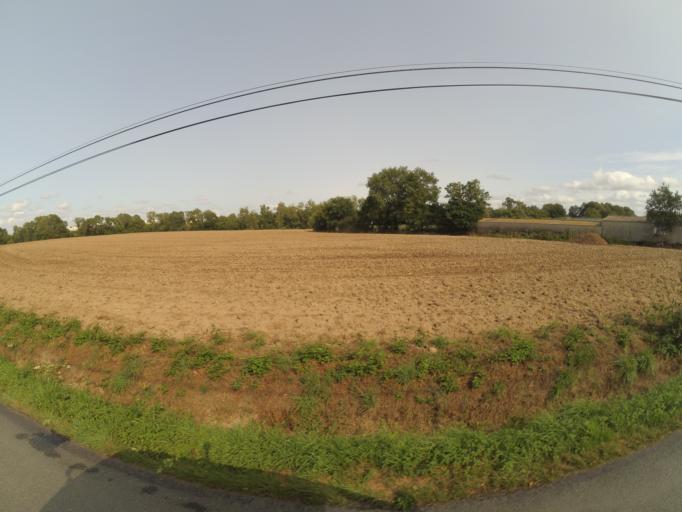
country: FR
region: Pays de la Loire
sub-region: Departement de la Vendee
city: La Bruffiere
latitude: 47.0052
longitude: -1.2013
